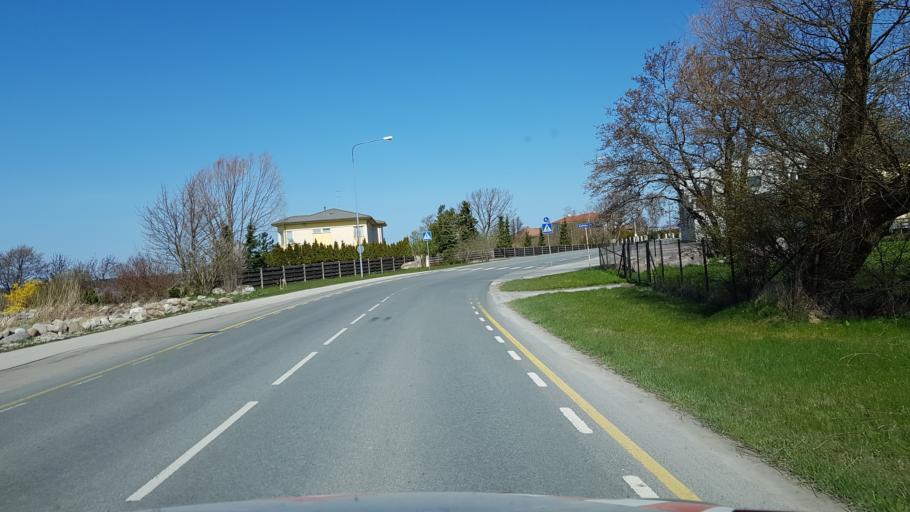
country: EE
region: Harju
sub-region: Viimsi vald
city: Rummu
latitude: 59.5544
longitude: 24.7939
